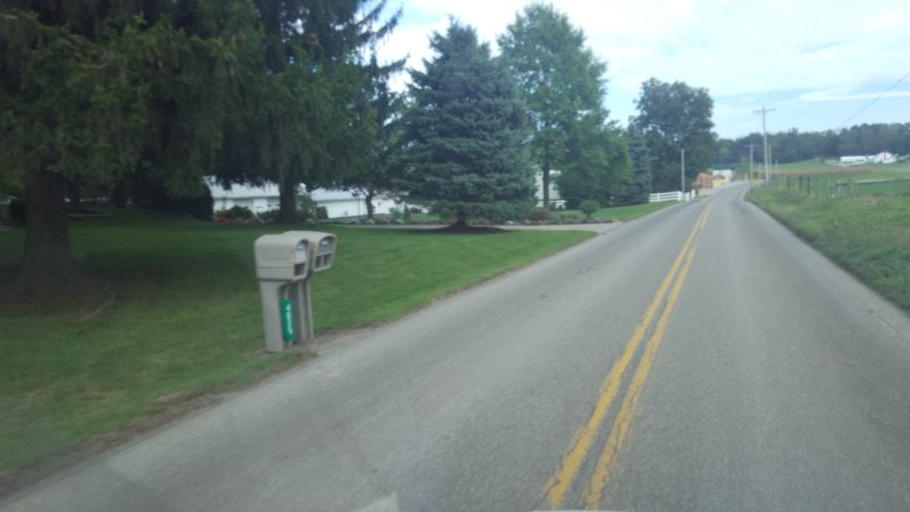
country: US
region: Ohio
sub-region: Holmes County
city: Millersburg
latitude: 40.5876
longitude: -81.7937
